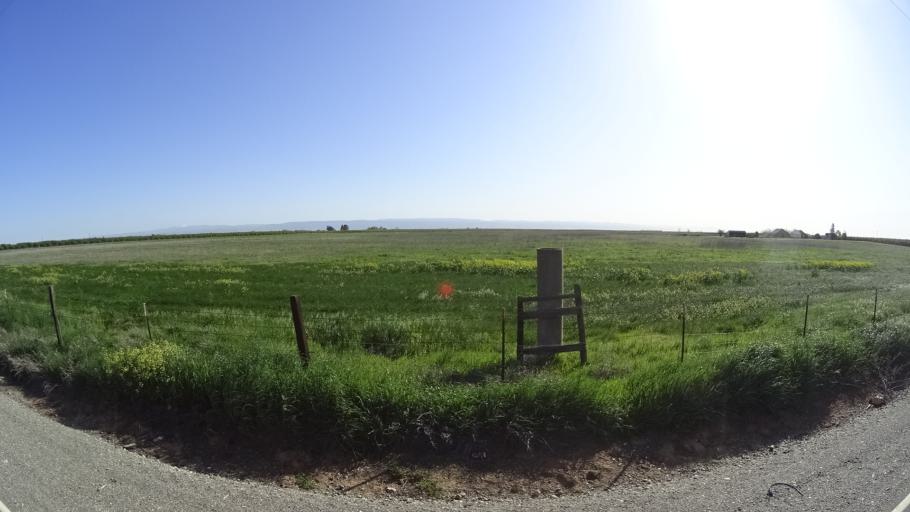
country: US
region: California
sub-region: Glenn County
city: Hamilton City
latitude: 39.7578
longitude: -122.1041
